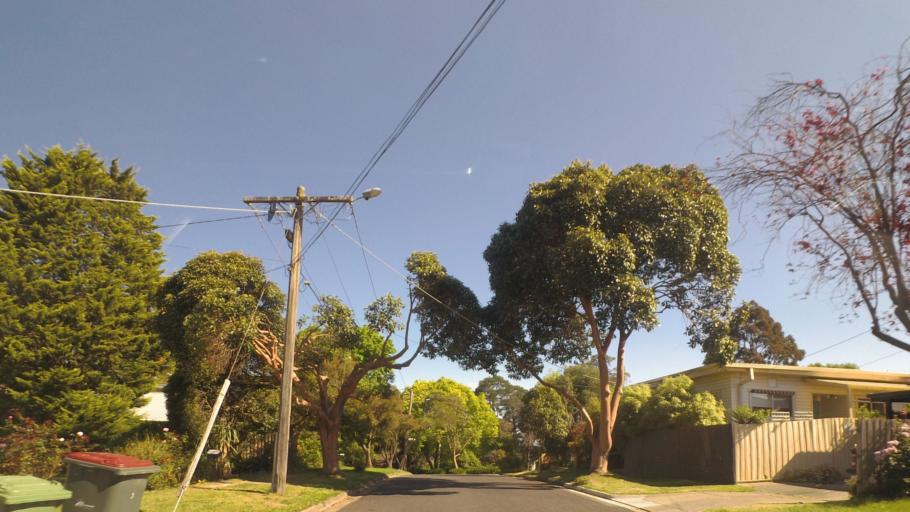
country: AU
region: Victoria
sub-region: Maroondah
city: Heathmont
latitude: -37.8262
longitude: 145.2497
